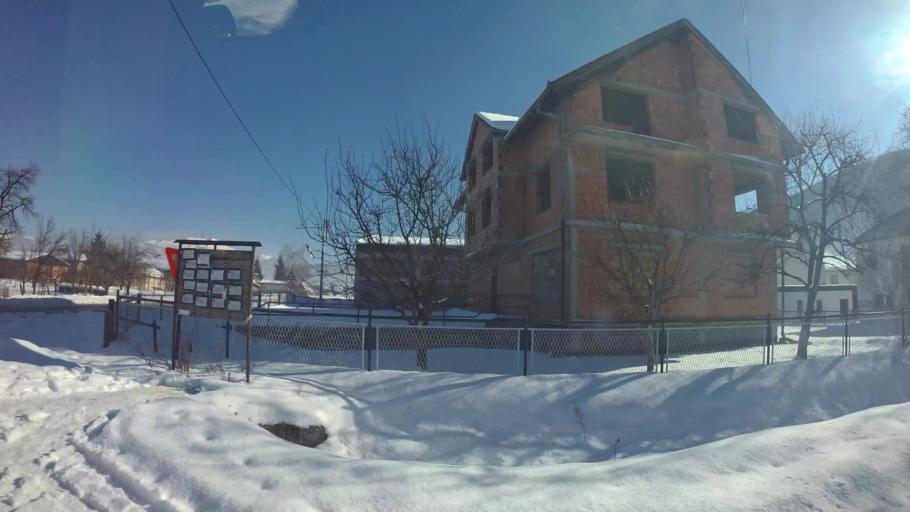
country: BA
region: Federation of Bosnia and Herzegovina
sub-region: Kanton Sarajevo
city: Sarajevo
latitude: 43.7909
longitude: 18.3382
